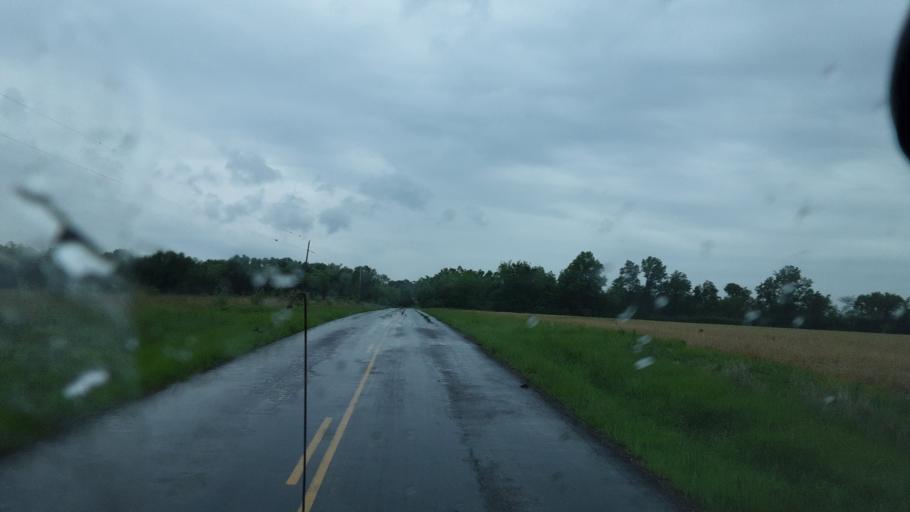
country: US
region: Missouri
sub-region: Randolph County
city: Moberly
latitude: 39.3894
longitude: -92.2486
